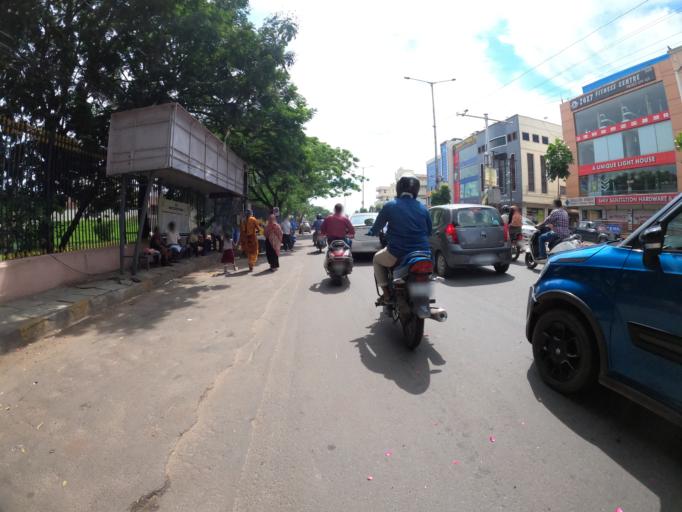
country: IN
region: Telangana
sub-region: Hyderabad
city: Hyderabad
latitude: 17.3730
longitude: 78.4139
